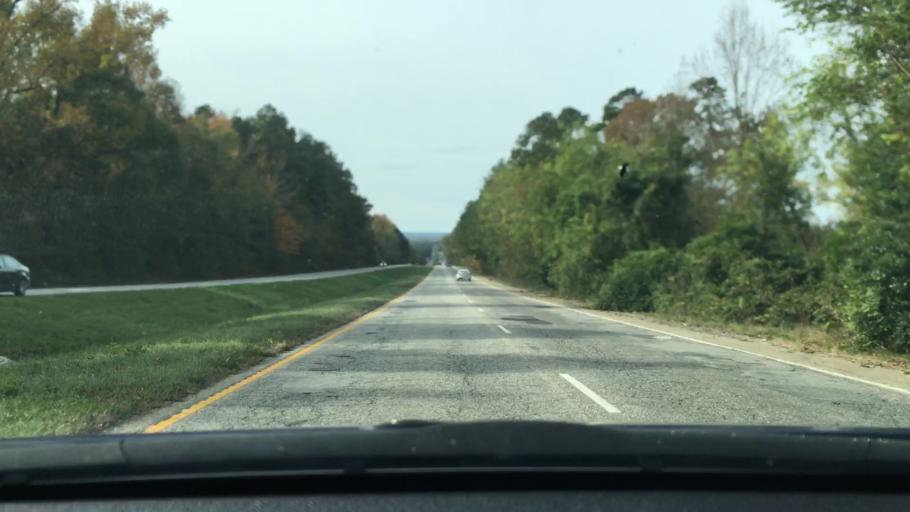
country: US
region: South Carolina
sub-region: Sumter County
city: Stateburg
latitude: 33.9466
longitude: -80.5372
